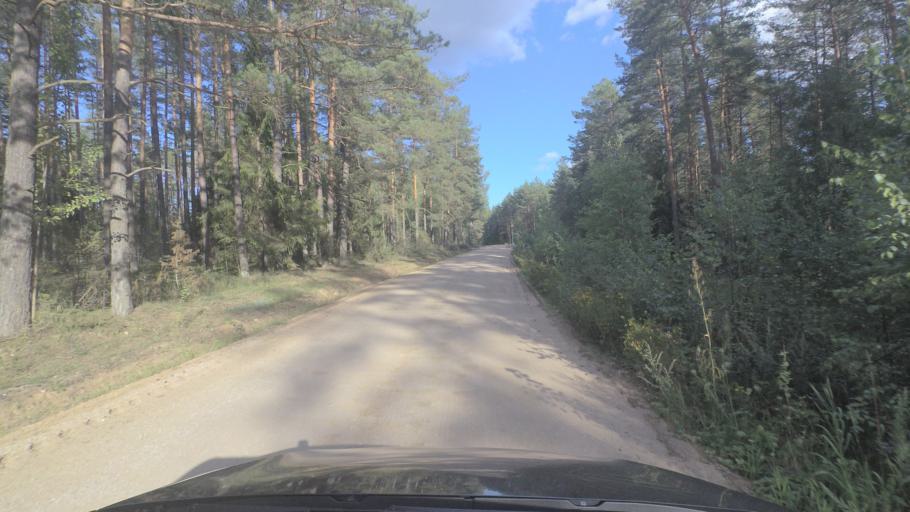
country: LT
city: Pabrade
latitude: 55.1541
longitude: 25.7794
